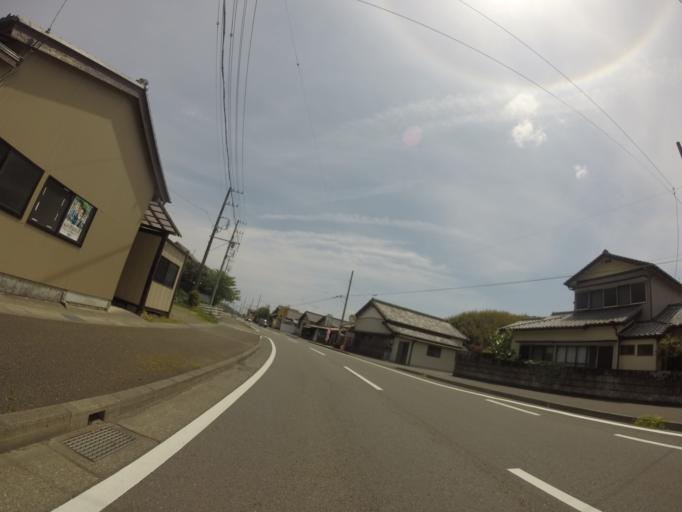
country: JP
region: Shizuoka
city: Fujieda
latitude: 34.8939
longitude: 138.2493
